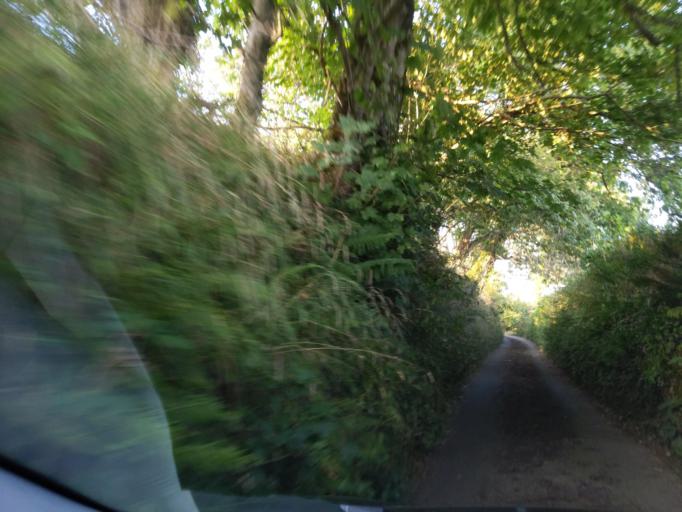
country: GB
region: England
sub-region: Cornwall
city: Fowey
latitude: 50.3662
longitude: -4.5926
